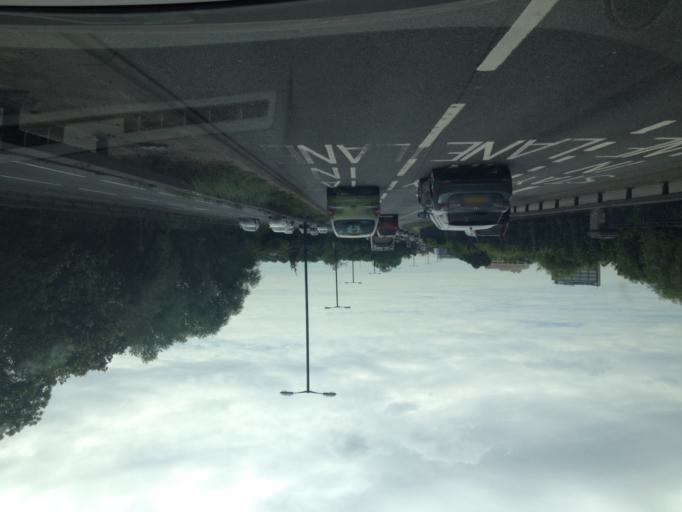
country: GB
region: England
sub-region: Greater London
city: Ealing Broadway
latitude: 51.5317
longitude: -0.3080
